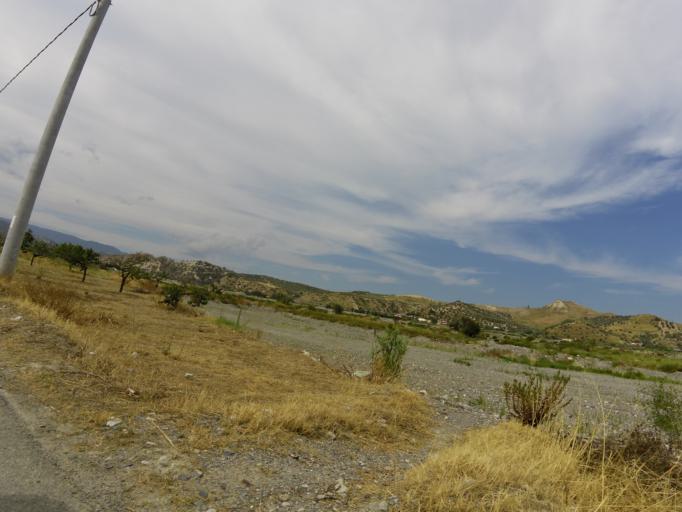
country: IT
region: Calabria
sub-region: Provincia di Reggio Calabria
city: Monasterace
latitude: 38.4504
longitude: 16.5209
